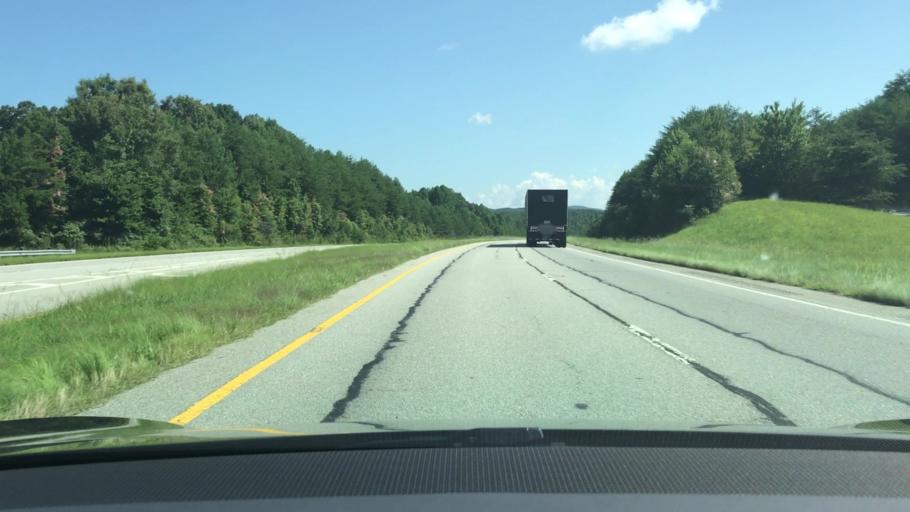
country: US
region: Georgia
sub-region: Habersham County
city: Clarkesville
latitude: 34.6903
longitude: -83.4238
